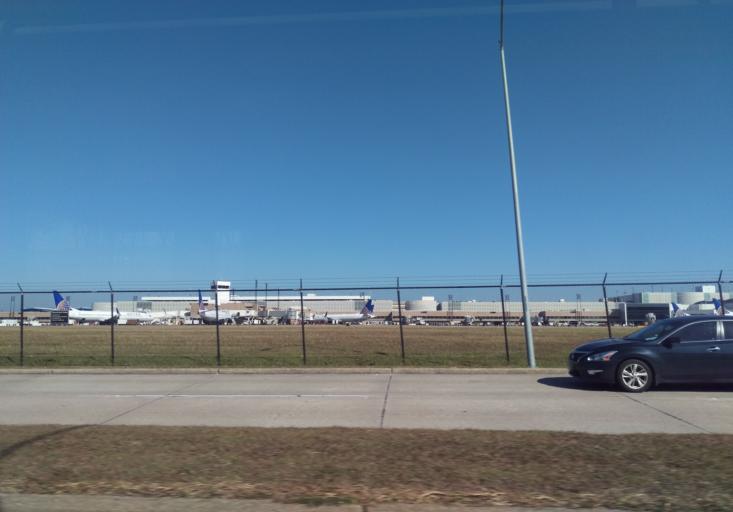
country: US
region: Texas
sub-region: Harris County
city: Aldine
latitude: 29.9818
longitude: -95.3377
